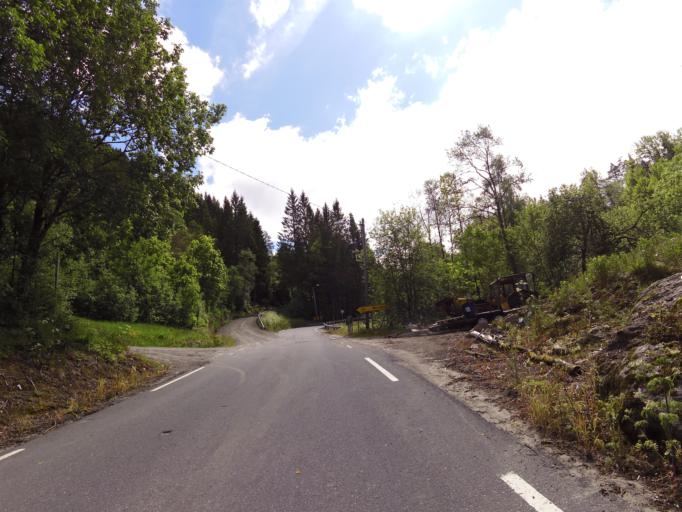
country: NO
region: Vest-Agder
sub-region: Kvinesdal
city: Liknes
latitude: 58.2878
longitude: 6.9392
